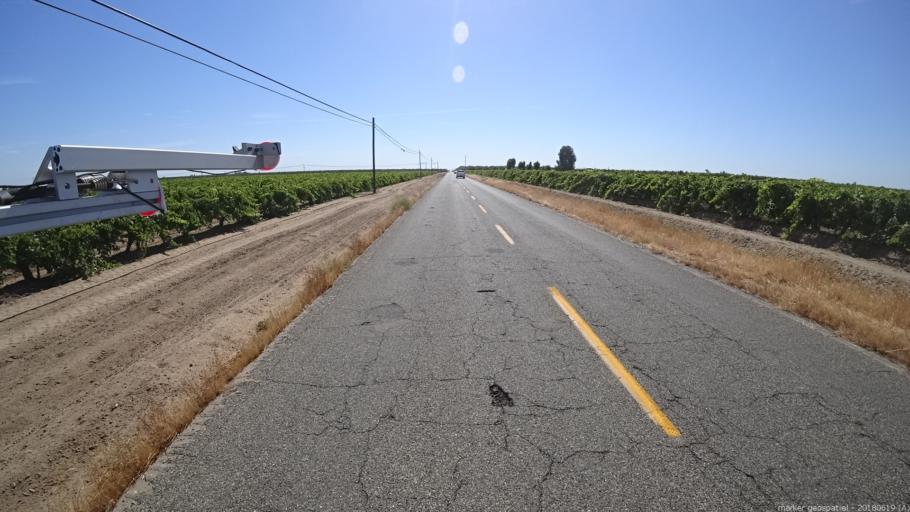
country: US
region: California
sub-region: Fresno County
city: Biola
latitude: 36.8368
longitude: -120.0945
